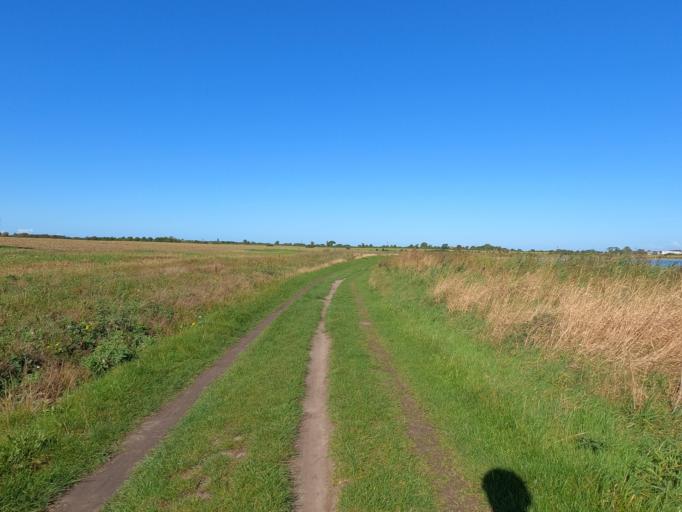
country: DE
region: Schleswig-Holstein
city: Grossenbrode
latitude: 54.3514
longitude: 11.0585
